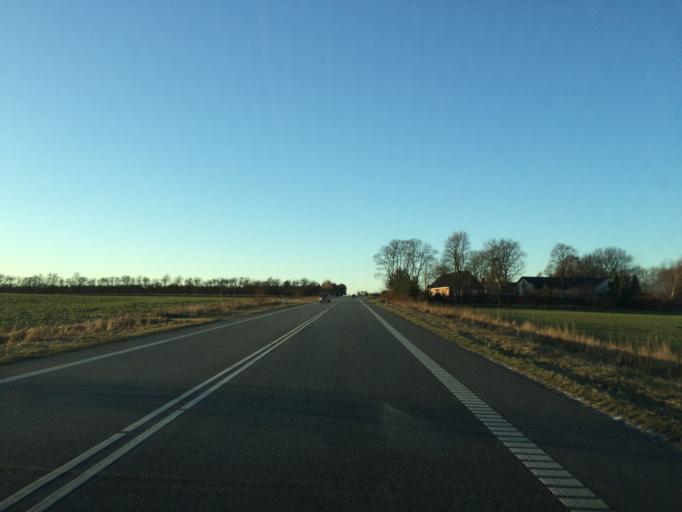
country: DK
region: Central Jutland
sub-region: Randers Kommune
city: Langa
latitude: 56.4741
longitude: 9.9362
